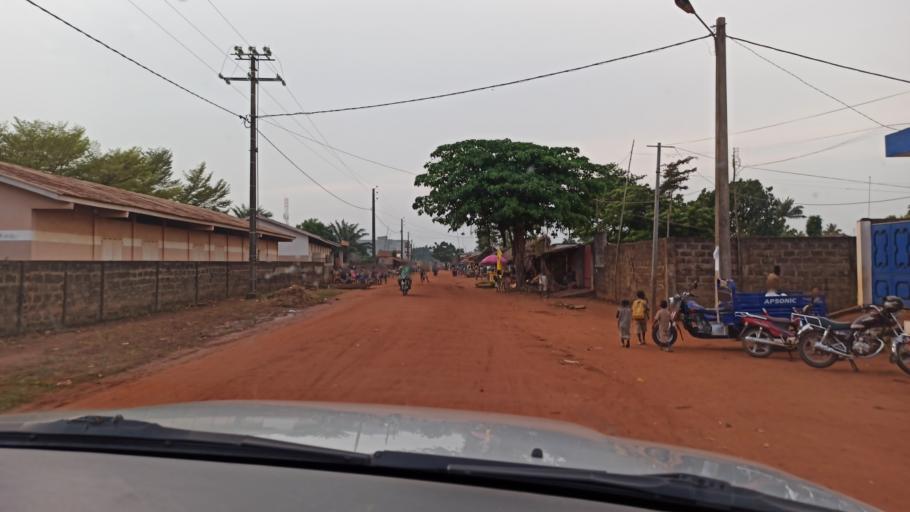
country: BJ
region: Queme
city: Porto-Novo
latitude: 6.5273
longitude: 2.6686
